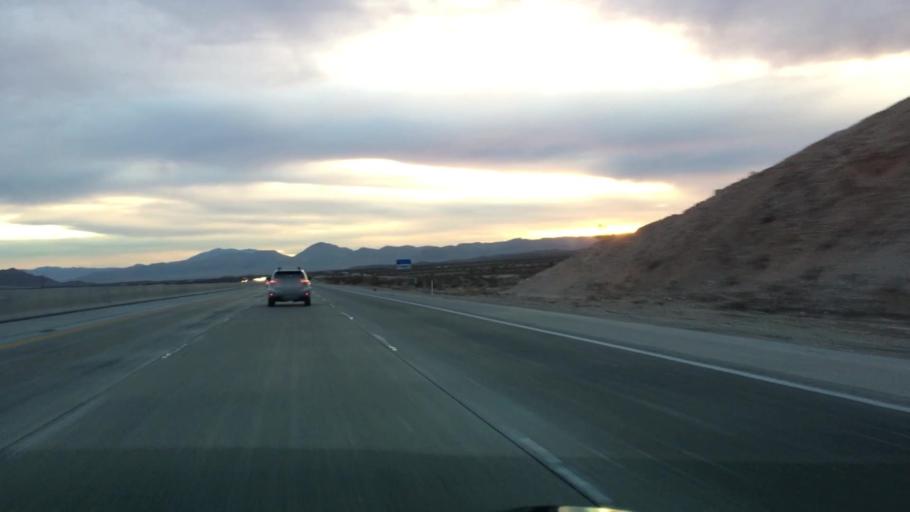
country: US
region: Nevada
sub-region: Clark County
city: Enterprise
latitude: 35.8662
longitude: -115.2487
